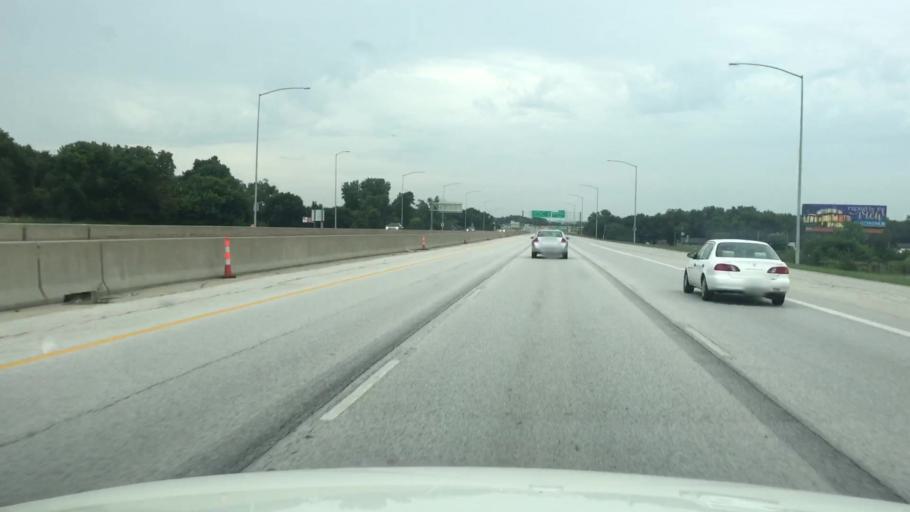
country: US
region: Iowa
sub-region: Polk County
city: Des Moines
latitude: 41.6258
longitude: -93.5756
